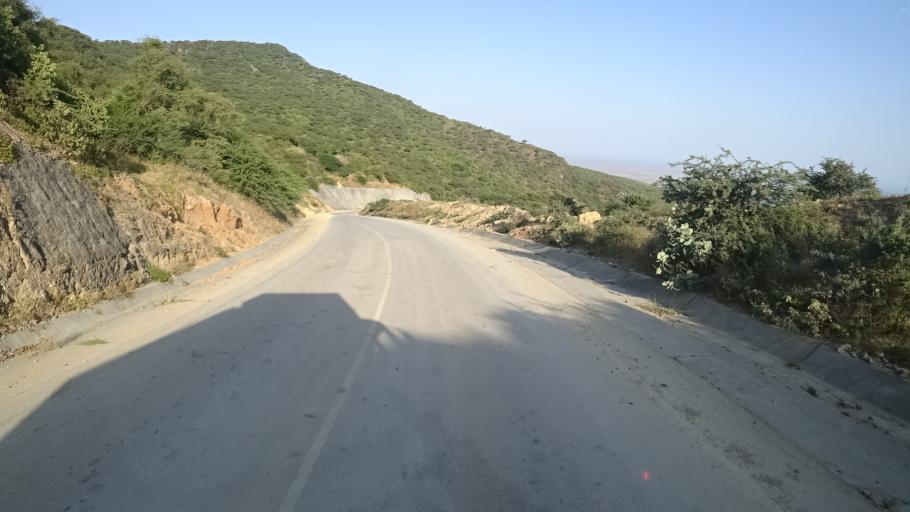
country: OM
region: Zufar
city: Salalah
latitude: 17.0611
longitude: 54.6068
